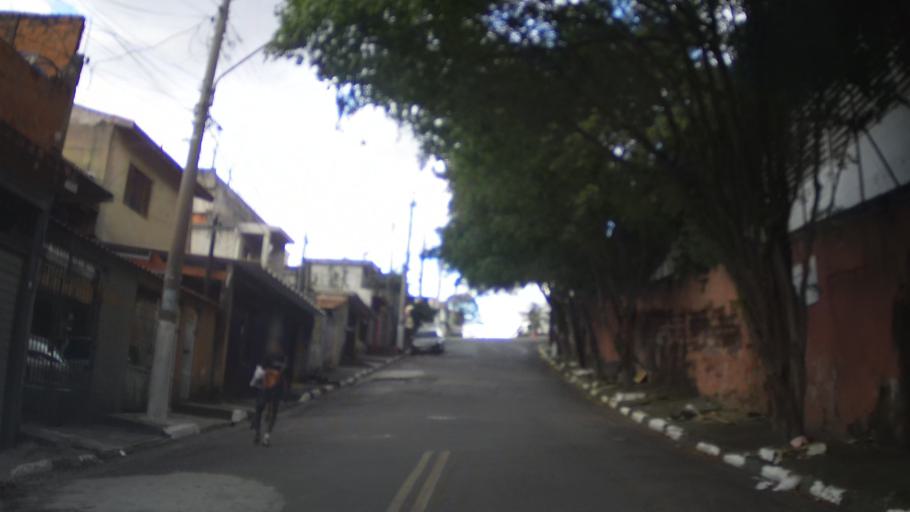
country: BR
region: Sao Paulo
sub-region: Guarulhos
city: Guarulhos
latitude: -23.4805
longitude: -46.5550
